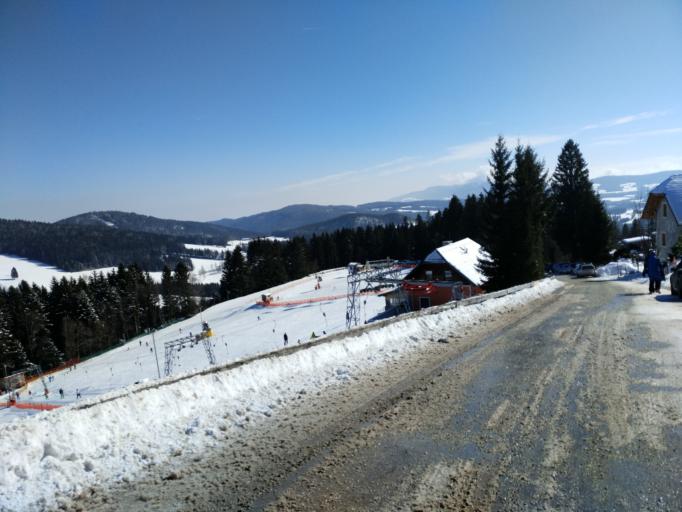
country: AT
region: Styria
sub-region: Politischer Bezirk Hartberg-Fuerstenfeld
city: Sankt Jakob im Walde
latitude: 47.4773
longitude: 15.7847
